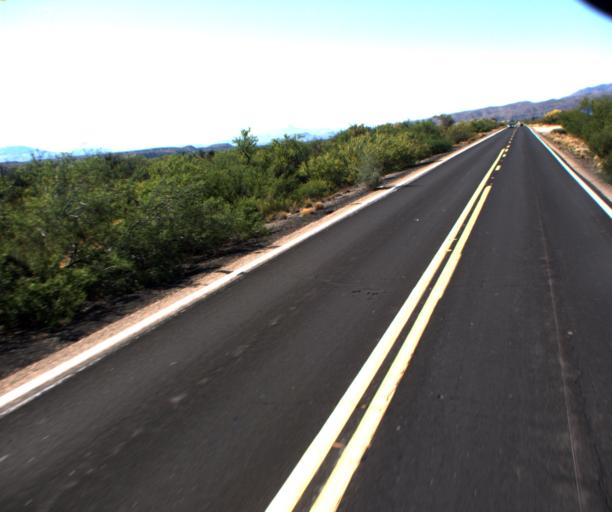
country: US
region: Arizona
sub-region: Yavapai County
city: Bagdad
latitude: 34.7345
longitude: -113.6153
